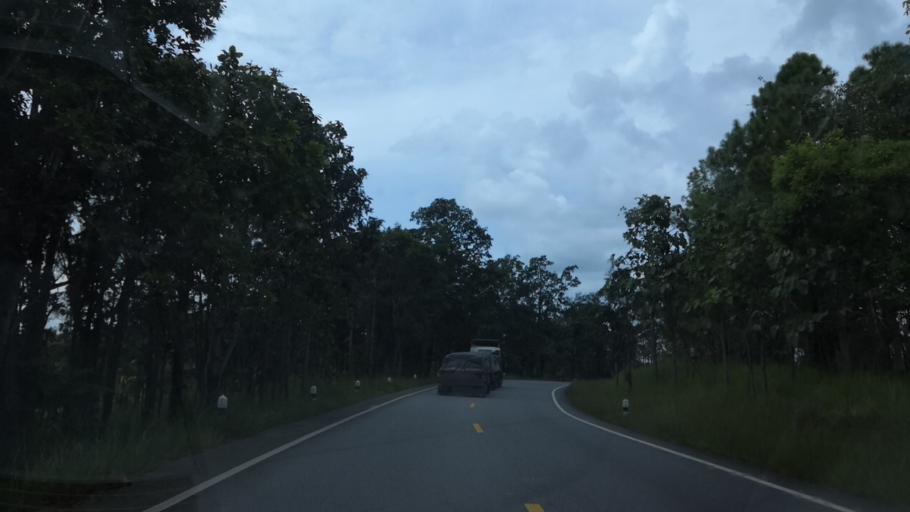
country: TH
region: Mae Hong Son
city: Khun Yuam
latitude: 18.7912
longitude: 97.9341
